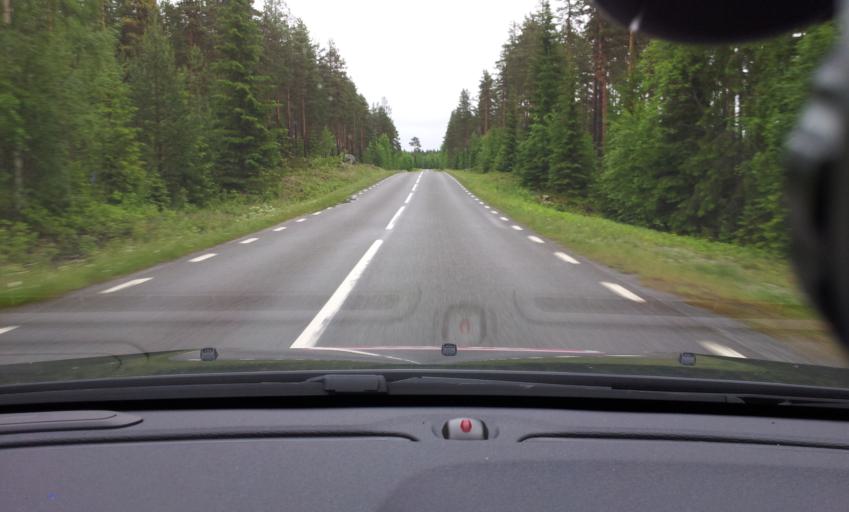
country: SE
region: Jaemtland
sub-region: Stroemsunds Kommun
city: Stroemsund
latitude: 63.4221
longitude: 15.5391
